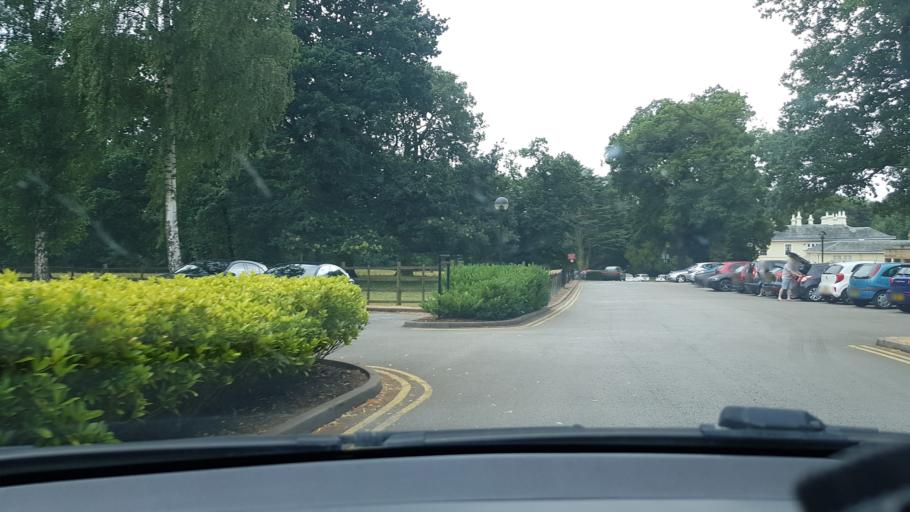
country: GB
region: England
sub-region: Nottinghamshire
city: Eastwood
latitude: 53.0251
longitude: -1.3093
